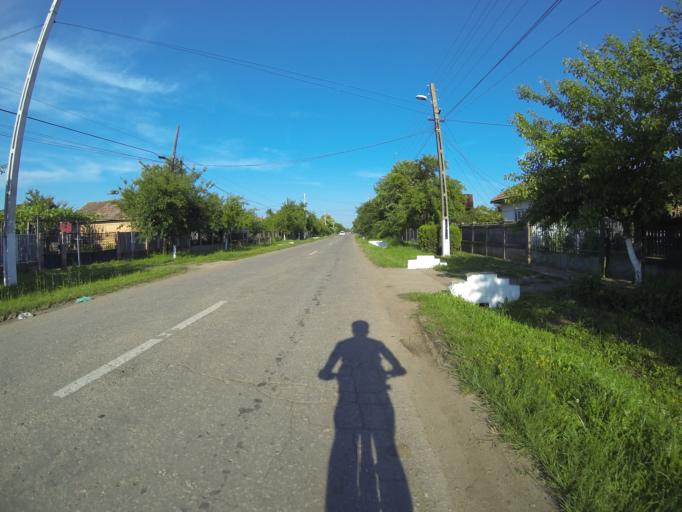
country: RO
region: Dolj
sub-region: Comuna Caloparu
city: Calopar
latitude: 44.1649
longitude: 23.7510
